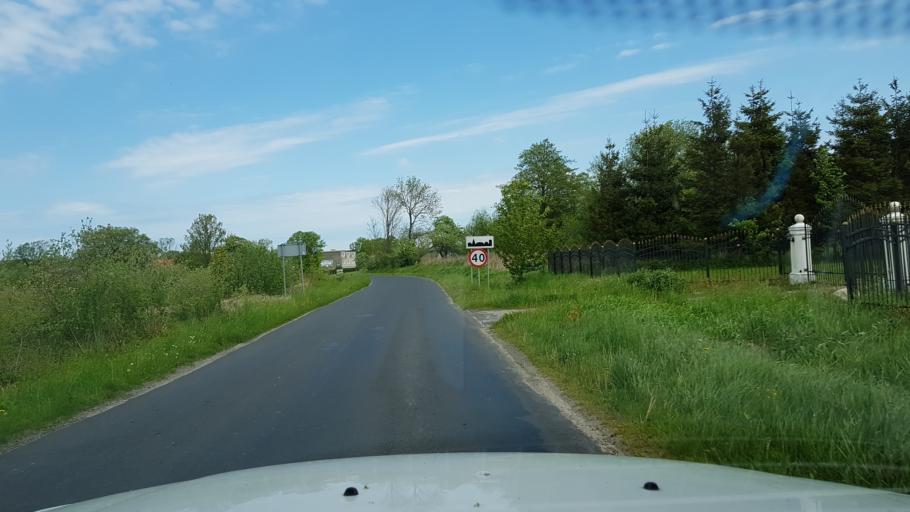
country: PL
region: West Pomeranian Voivodeship
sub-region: Powiat koszalinski
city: Mielno
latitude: 54.2469
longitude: 16.0084
